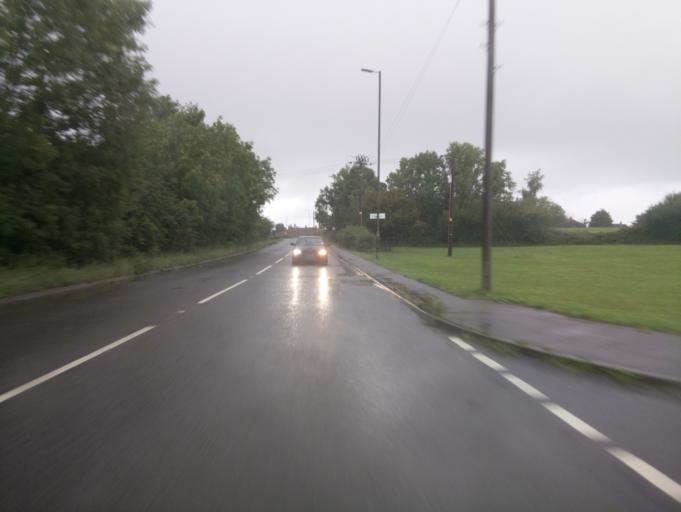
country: GB
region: England
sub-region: Gloucestershire
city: Tewkesbury
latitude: 51.9798
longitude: -2.1551
